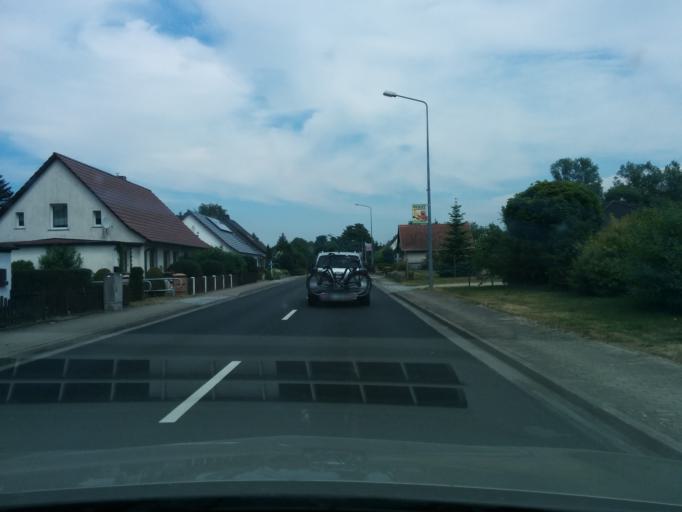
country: DE
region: Mecklenburg-Vorpommern
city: Zussow
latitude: 54.0102
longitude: 13.6428
